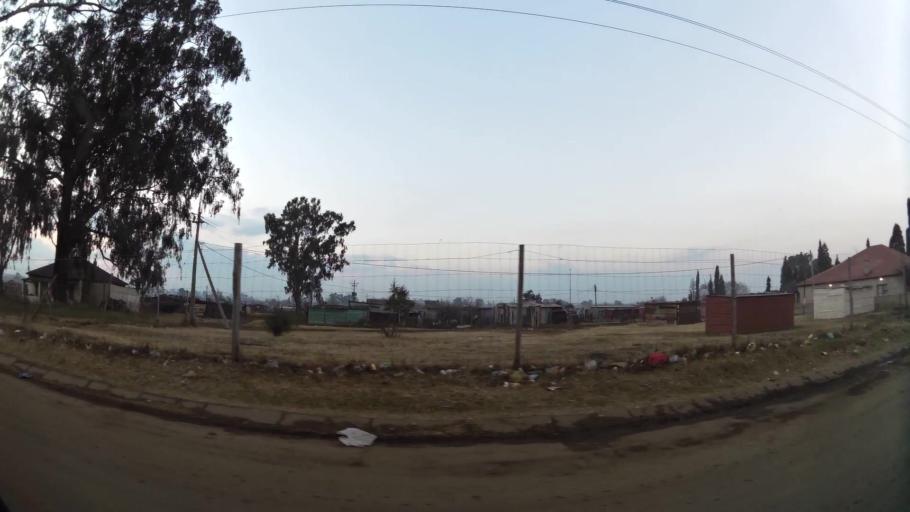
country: ZA
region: Gauteng
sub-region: City of Johannesburg Metropolitan Municipality
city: Orange Farm
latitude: -26.5469
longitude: 27.8458
